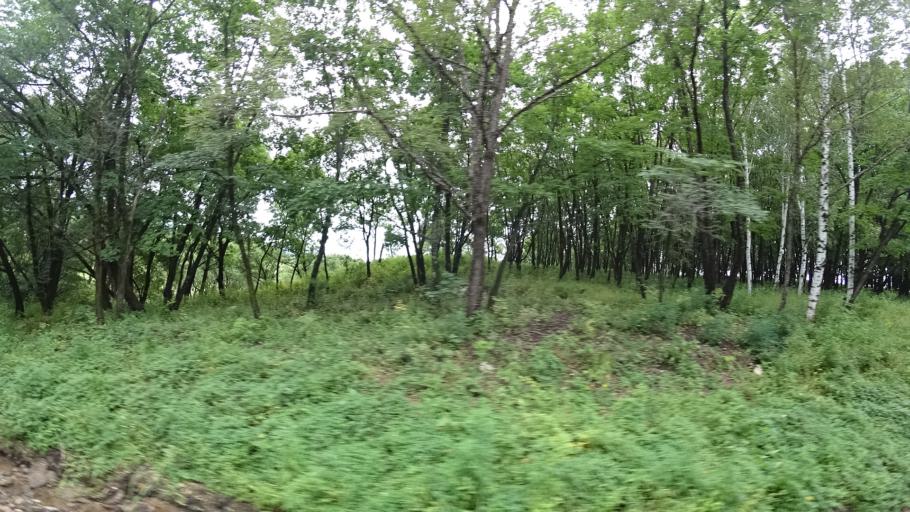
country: RU
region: Primorskiy
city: Rettikhovka
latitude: 44.0658
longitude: 132.6488
